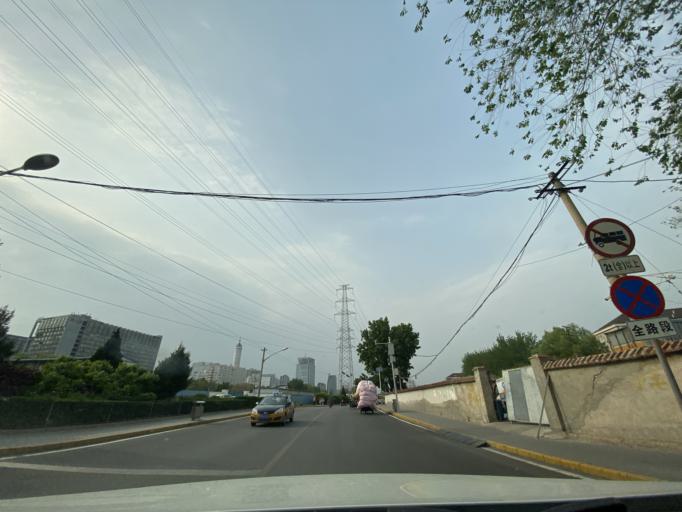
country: CN
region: Beijing
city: Haidian
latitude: 39.9772
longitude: 116.3353
